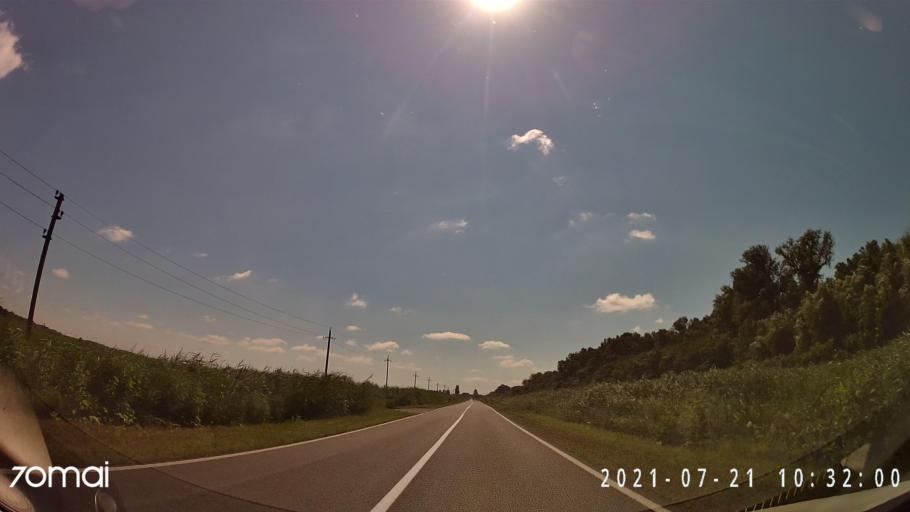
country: RO
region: Tulcea
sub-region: Oras Isaccea
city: Isaccea
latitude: 45.3048
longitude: 28.4133
